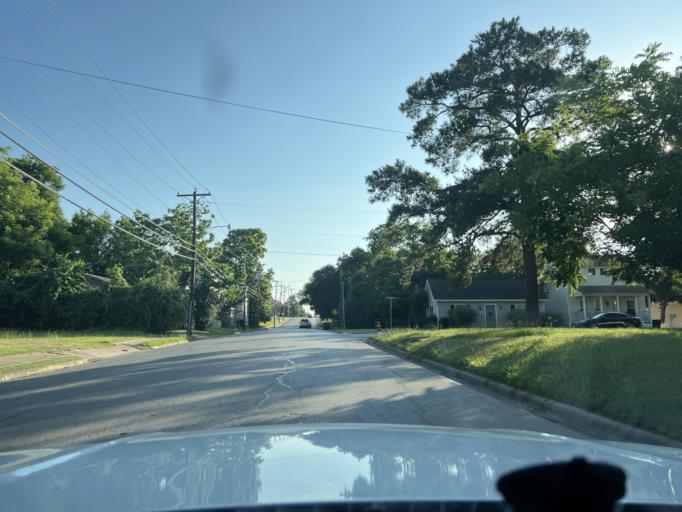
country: US
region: Texas
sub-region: Washington County
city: Brenham
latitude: 30.1715
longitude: -96.3950
